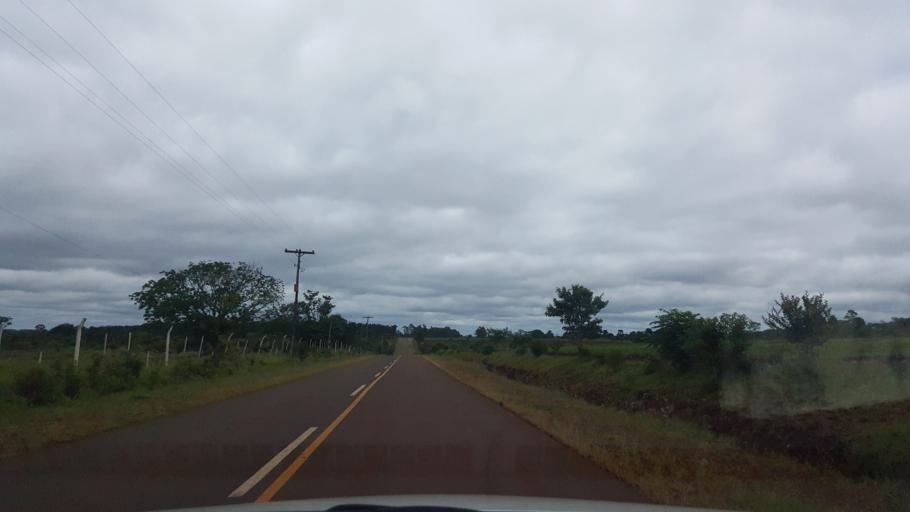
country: AR
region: Misiones
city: Ruiz de Montoya
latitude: -26.9686
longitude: -55.0692
